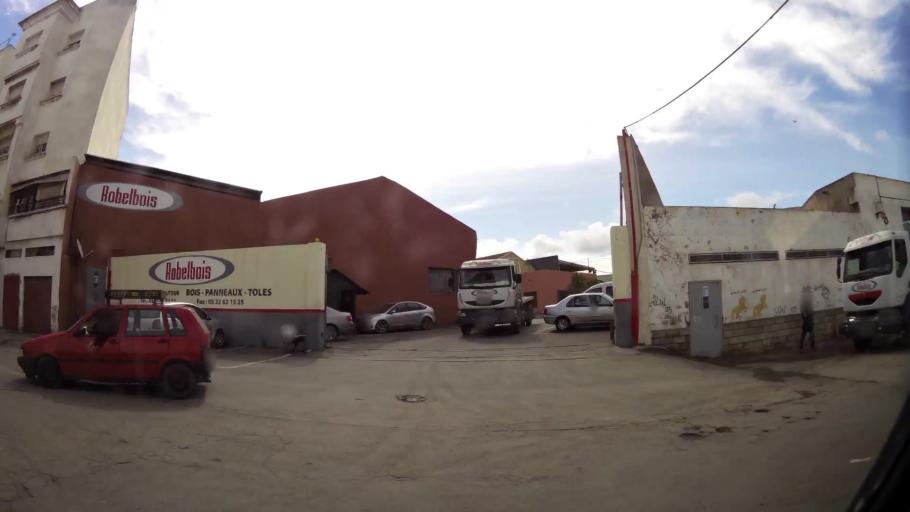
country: MA
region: Grand Casablanca
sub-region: Casablanca
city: Casablanca
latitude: 33.5818
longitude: -7.5752
